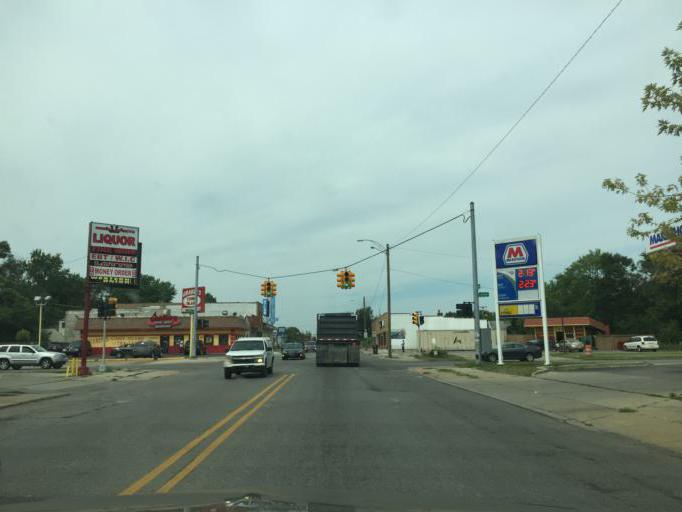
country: US
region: Michigan
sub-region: Wayne County
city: Redford
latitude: 42.4003
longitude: -83.2562
